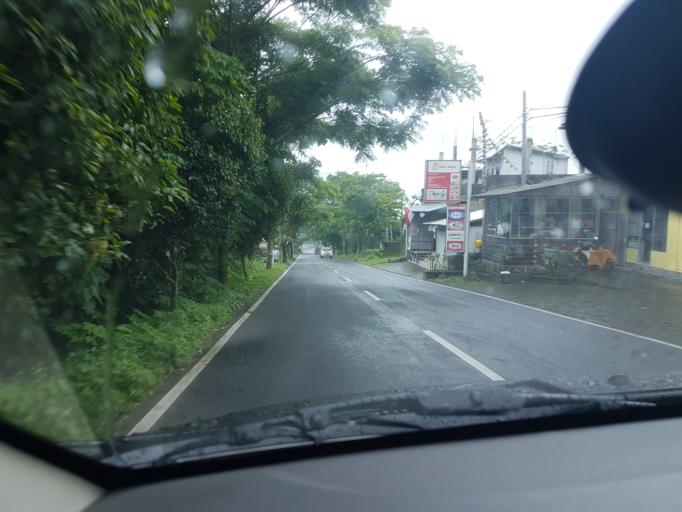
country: ID
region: Bali
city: Banjar Kedisan
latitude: -8.3001
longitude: 115.3552
